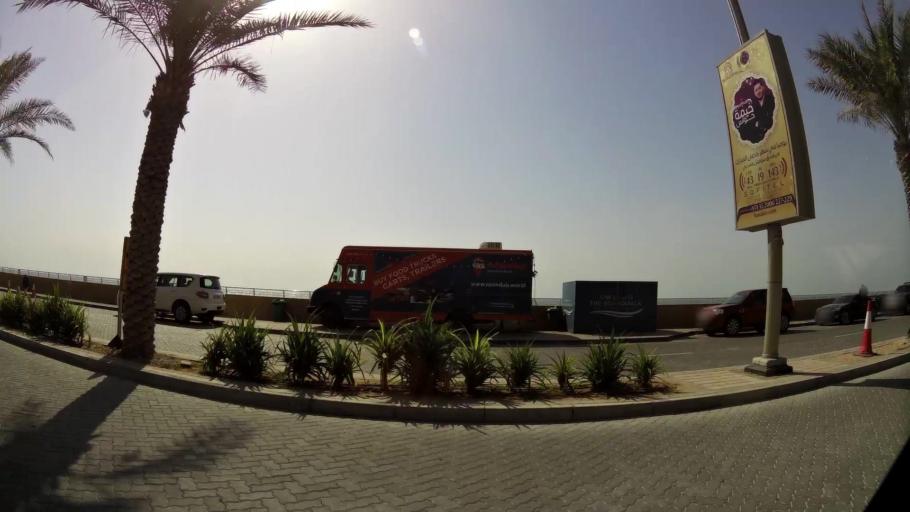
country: AE
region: Dubai
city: Dubai
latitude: 25.1307
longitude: 55.1154
